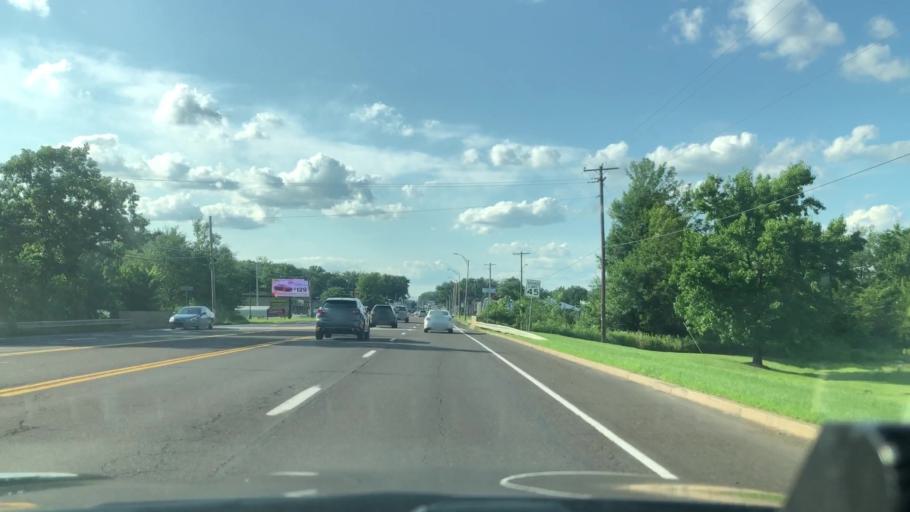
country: US
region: Pennsylvania
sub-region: Bucks County
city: Quakertown
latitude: 40.4260
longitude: -75.3482
